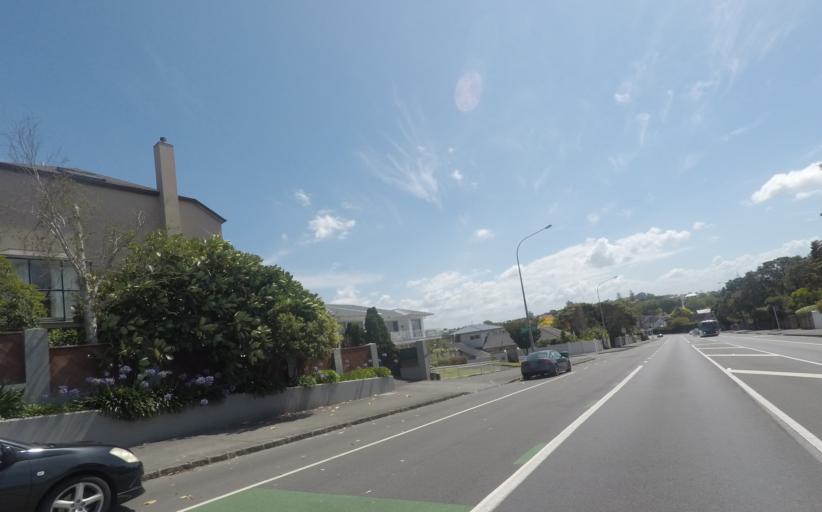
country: NZ
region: Auckland
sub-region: Auckland
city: Tamaki
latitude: -36.8796
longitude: 174.8208
